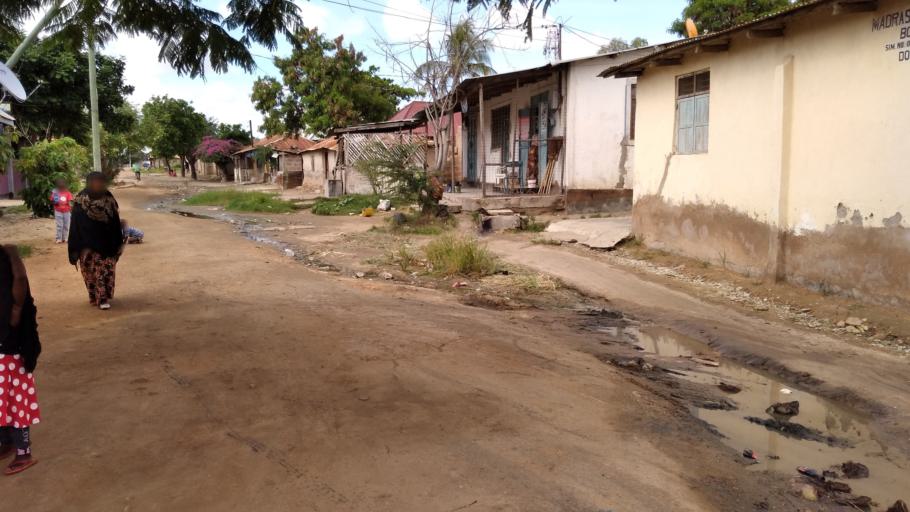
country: TZ
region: Dodoma
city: Dodoma
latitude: -6.1582
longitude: 35.7396
